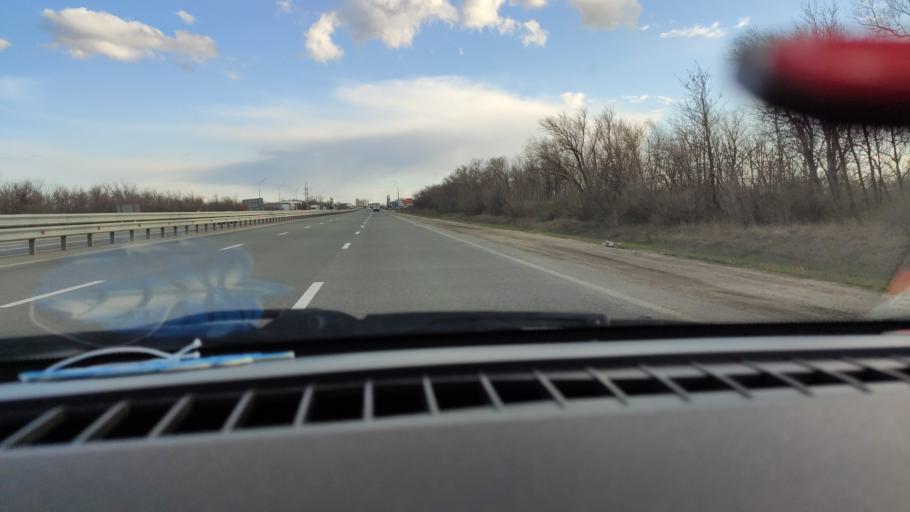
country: RU
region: Saratov
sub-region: Saratovskiy Rayon
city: Saratov
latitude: 51.6590
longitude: 45.9988
